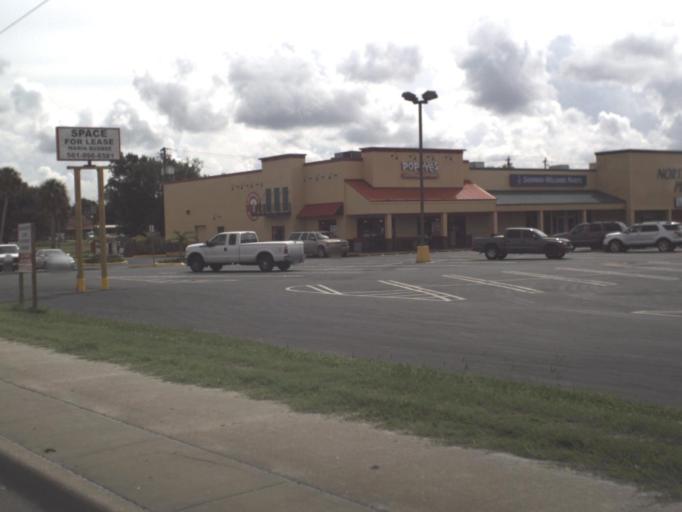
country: US
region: Florida
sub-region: Okeechobee County
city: Okeechobee
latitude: 27.2437
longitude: -80.8213
